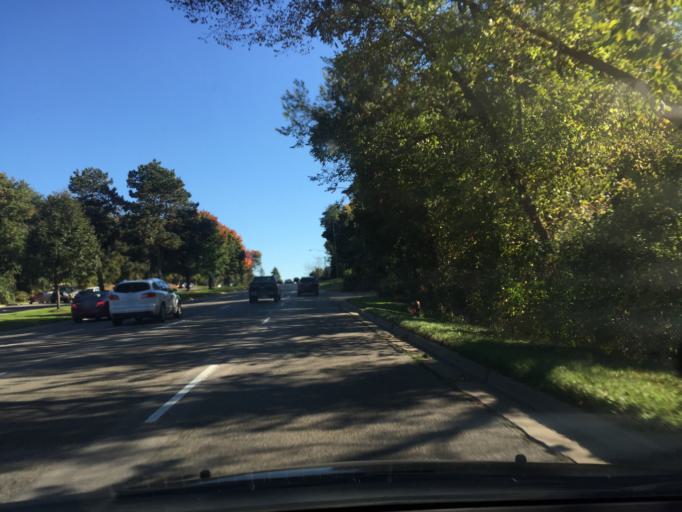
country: US
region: Michigan
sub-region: Oakland County
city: Bloomfield Hills
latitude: 42.5810
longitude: -83.2429
